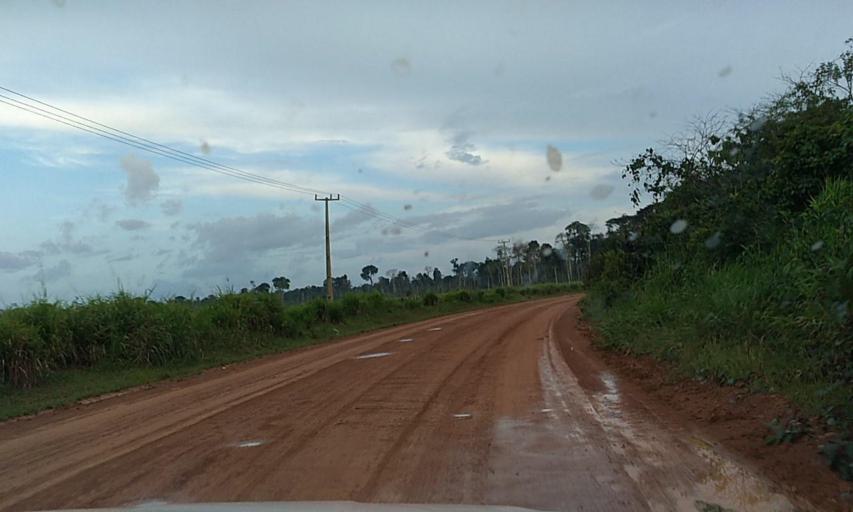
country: BR
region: Para
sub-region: Senador Jose Porfirio
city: Senador Jose Porfirio
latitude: -2.7044
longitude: -51.8134
